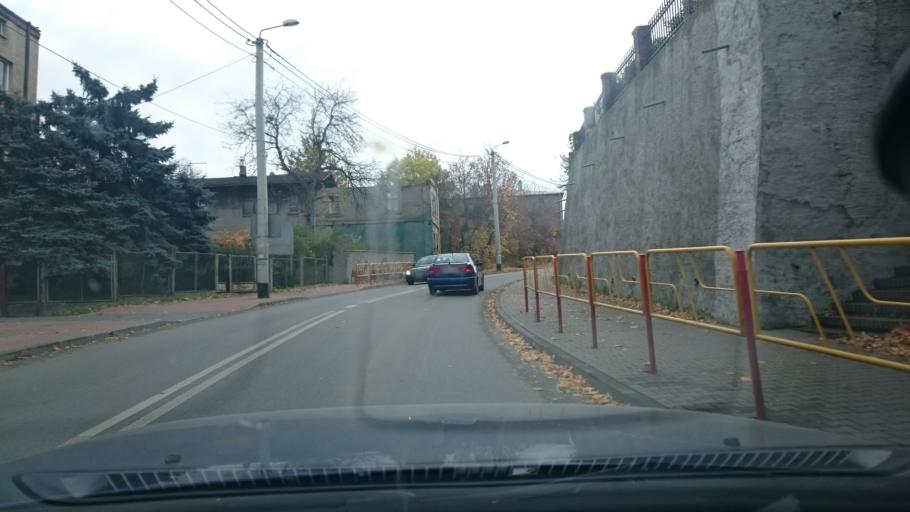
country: PL
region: Silesian Voivodeship
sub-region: Powiat bedzinski
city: Czeladz
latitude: 50.3487
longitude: 19.0913
